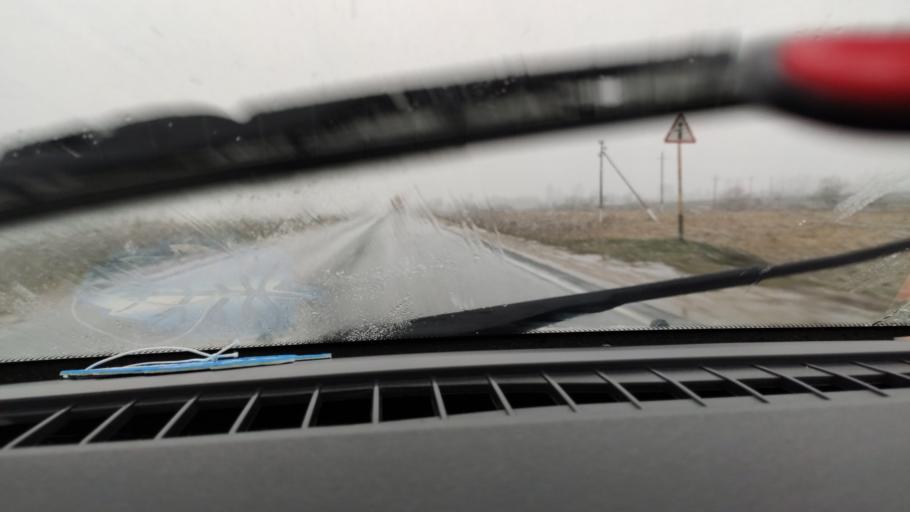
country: RU
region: Tatarstan
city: Cheremshan
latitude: 54.7169
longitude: 51.2245
